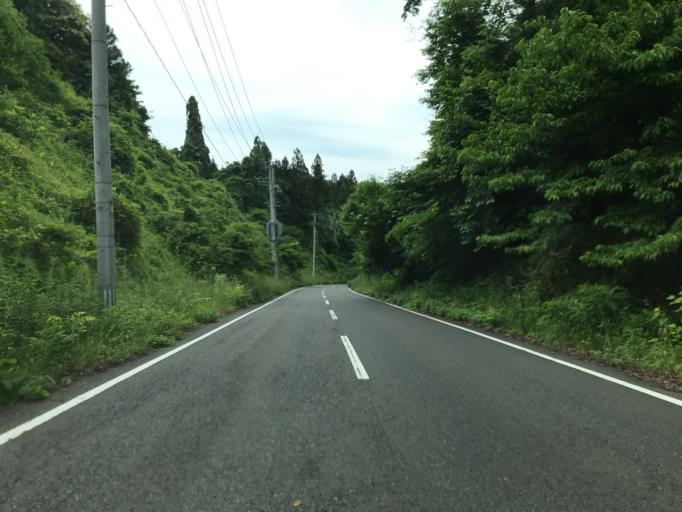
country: JP
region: Fukushima
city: Funehikimachi-funehiki
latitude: 37.4108
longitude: 140.6481
